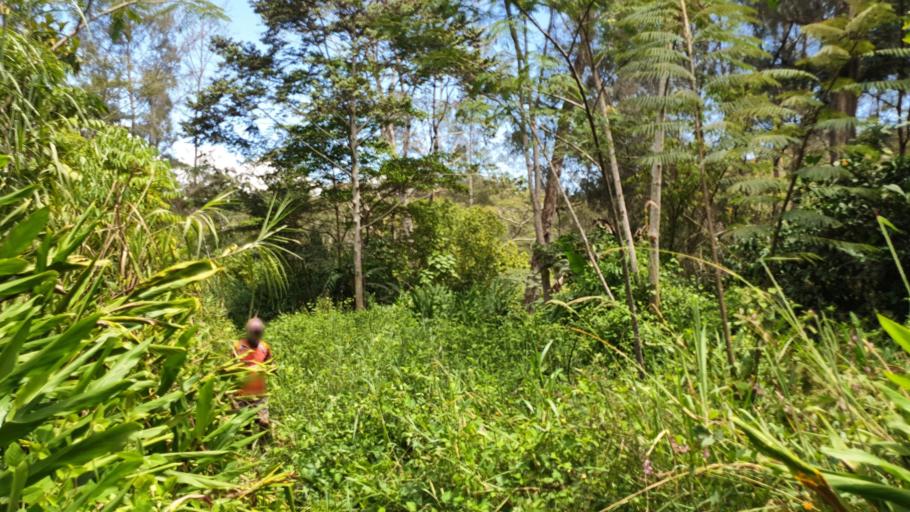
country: PG
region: Jiwaka
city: Minj
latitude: -5.9134
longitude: 144.8304
